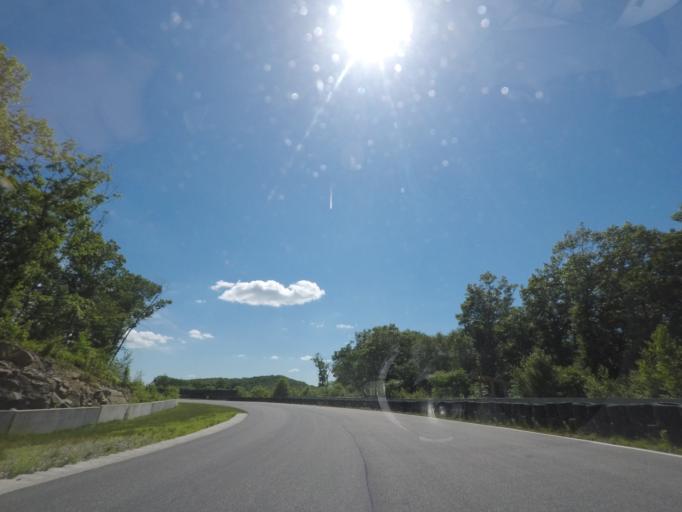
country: US
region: Massachusetts
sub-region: Hampshire County
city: Ware
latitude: 42.2388
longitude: -72.2427
